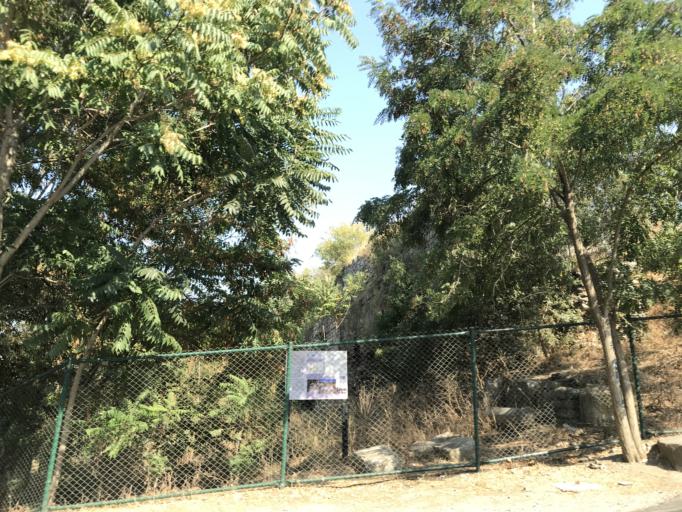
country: TR
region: Izmir
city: Selcuk
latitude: 37.9481
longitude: 27.3448
